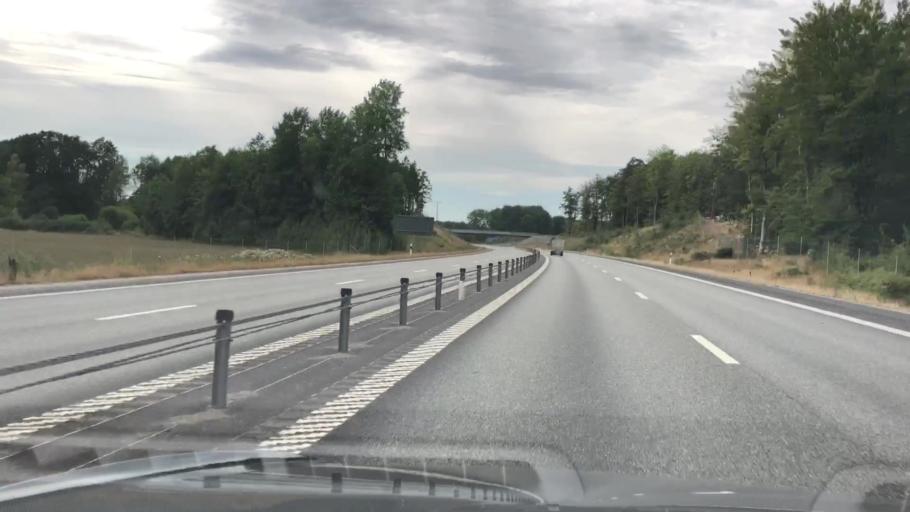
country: SE
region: Blekinge
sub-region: Karlshamns Kommun
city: Morrum
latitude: 56.1734
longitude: 14.6857
